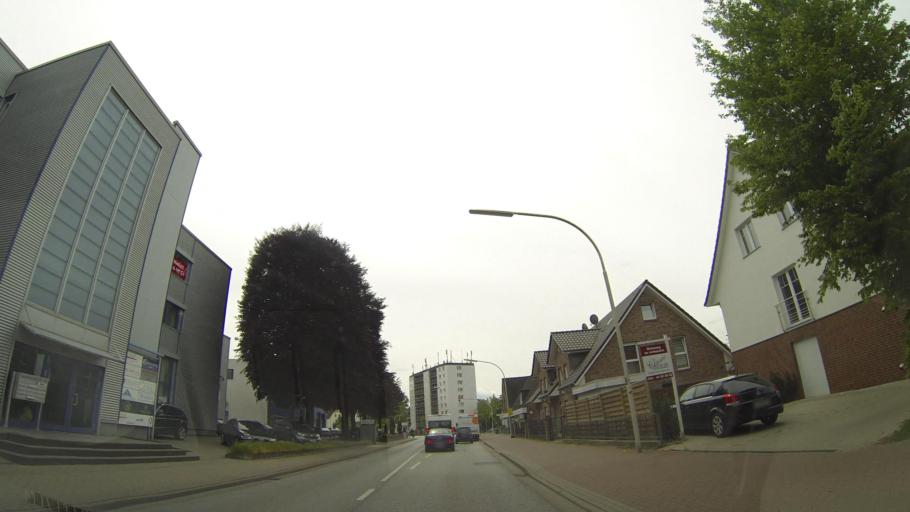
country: DE
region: Schleswig-Holstein
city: Halstenbek
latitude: 53.6094
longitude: 9.8398
